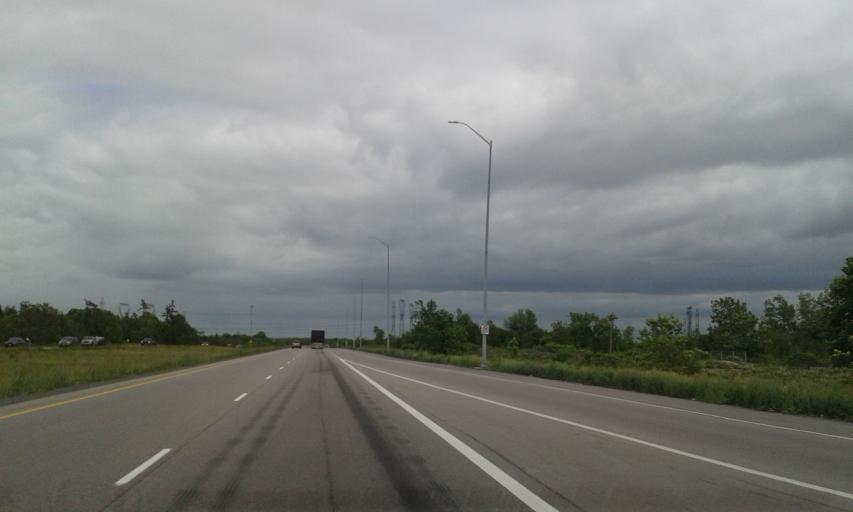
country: CA
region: Ontario
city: Kingston
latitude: 44.2851
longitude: -76.6528
